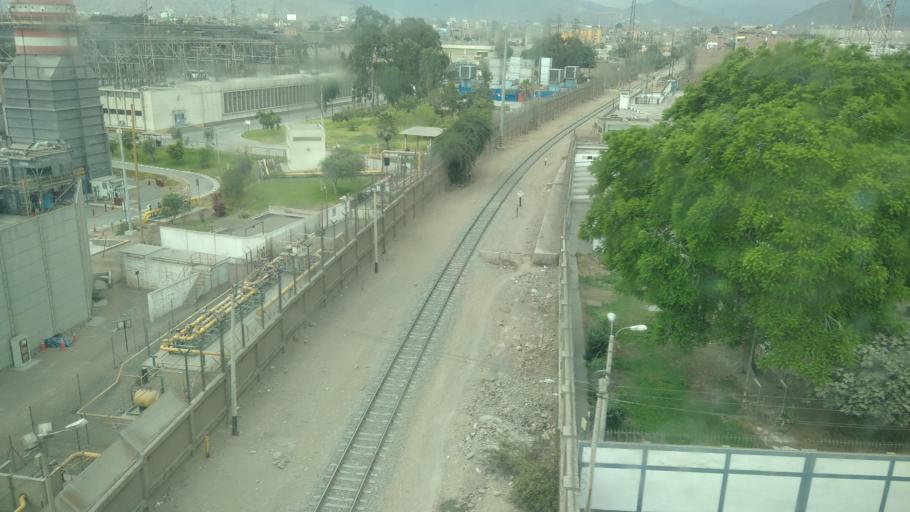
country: PE
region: Lima
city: Lima
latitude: -12.0411
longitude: -77.0123
